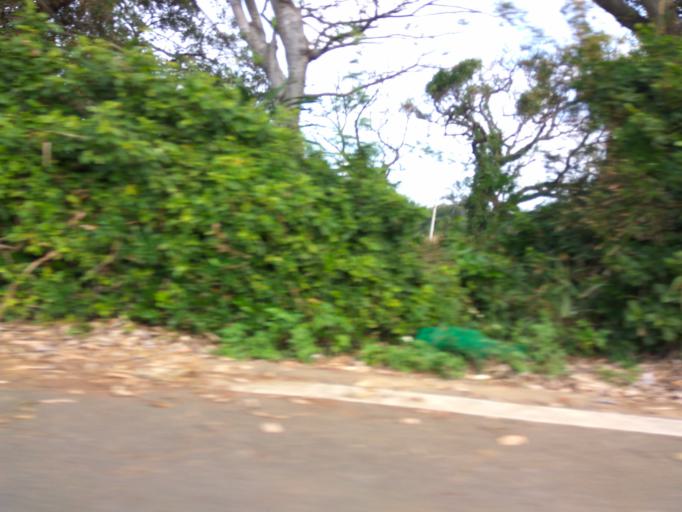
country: TW
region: Taiwan
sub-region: Hsinchu
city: Zhubei
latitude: 24.9506
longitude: 121.0007
